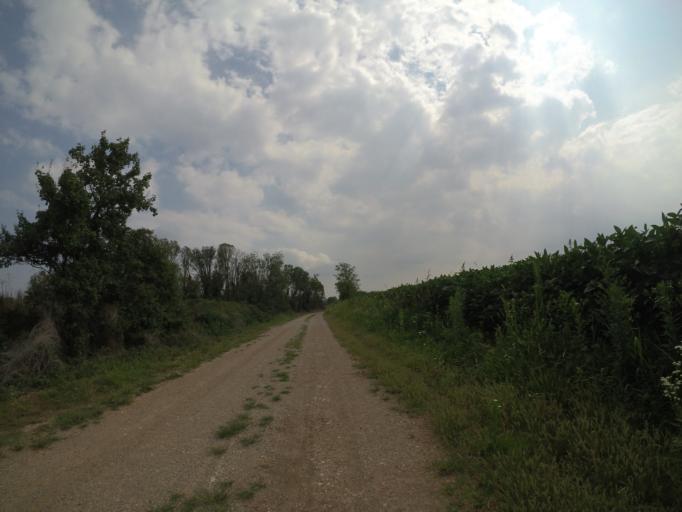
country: IT
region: Friuli Venezia Giulia
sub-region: Provincia di Udine
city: Codroipo
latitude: 45.9747
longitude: 13.0050
